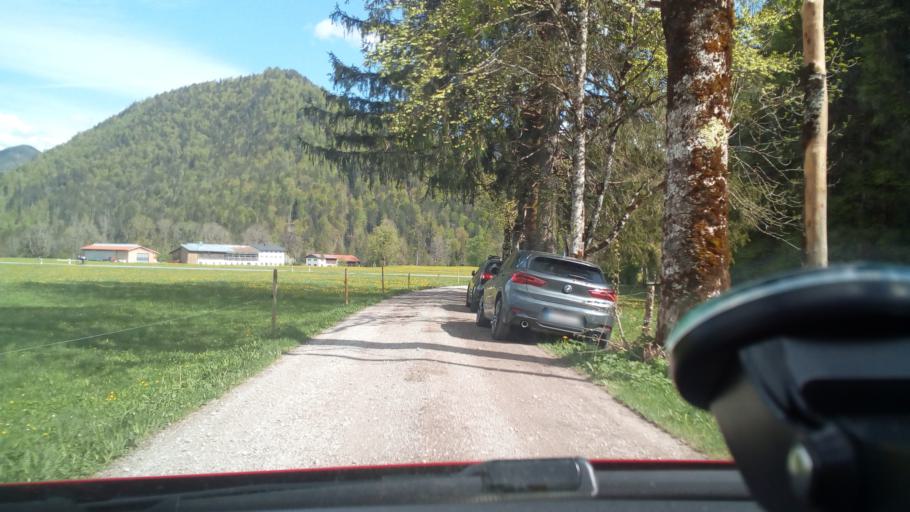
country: DE
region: Bavaria
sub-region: Upper Bavaria
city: Jachenau
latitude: 47.6172
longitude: 11.4999
